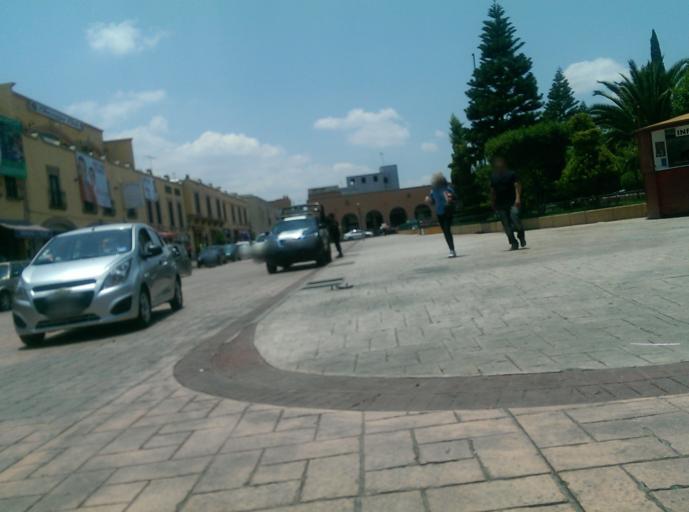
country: MX
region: Hidalgo
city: Actopan
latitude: 20.2682
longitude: -98.9450
